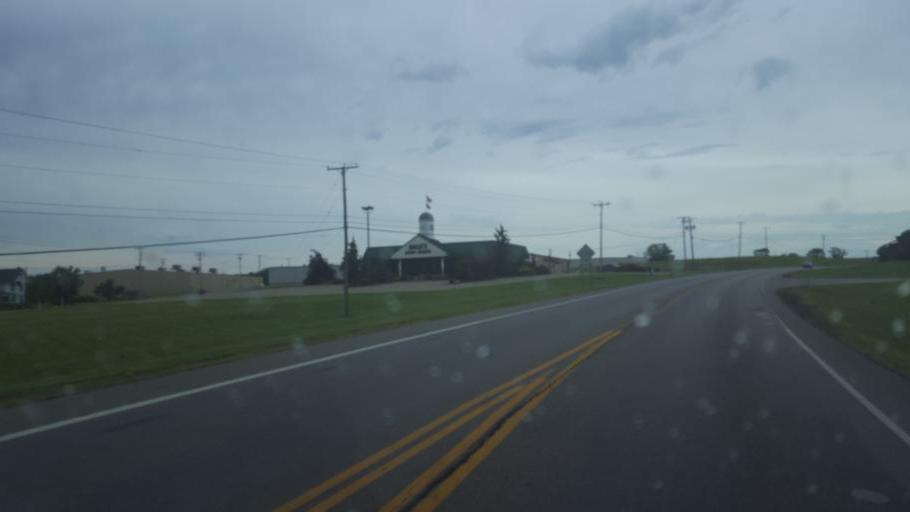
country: US
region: Ohio
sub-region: Richland County
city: Lincoln Heights
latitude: 40.7952
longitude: -82.5126
